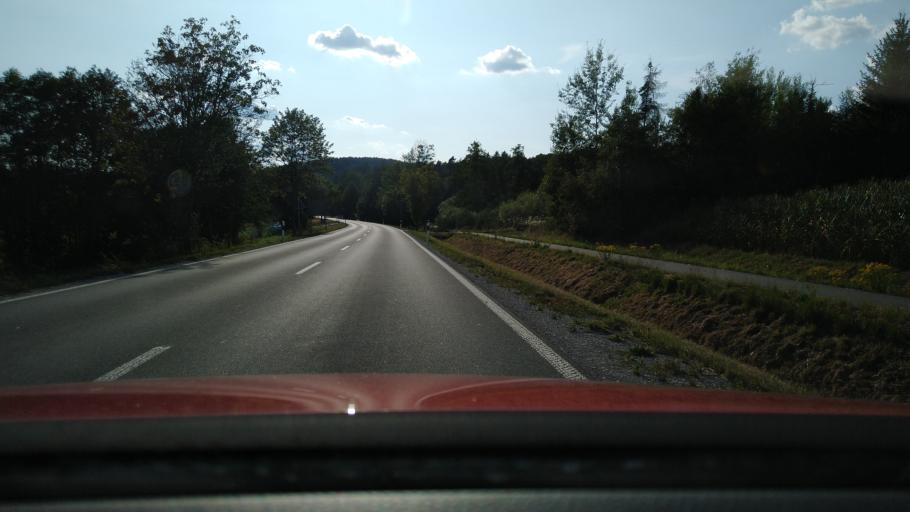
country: DE
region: Bavaria
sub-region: Upper Franconia
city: Glashutten
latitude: 49.9233
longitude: 11.4208
